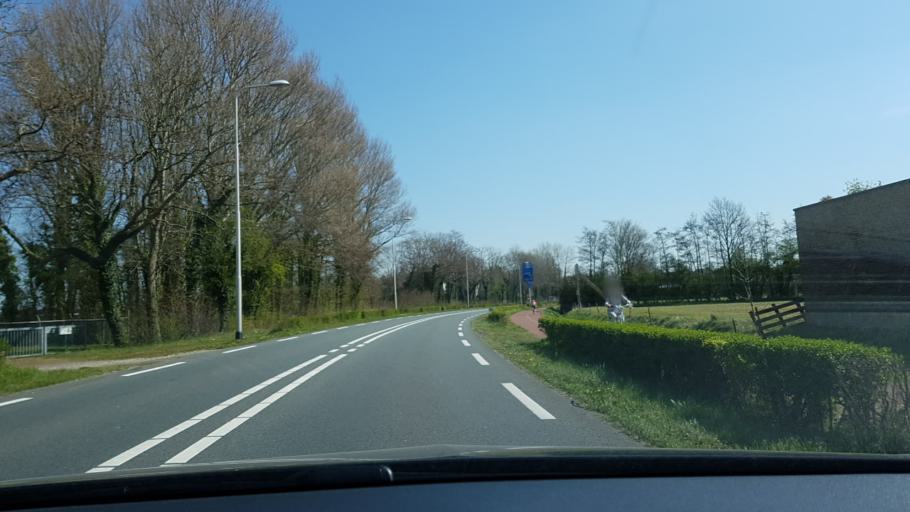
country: NL
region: South Holland
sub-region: Gemeente Teylingen
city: Sassenheim
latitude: 52.2324
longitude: 4.5232
